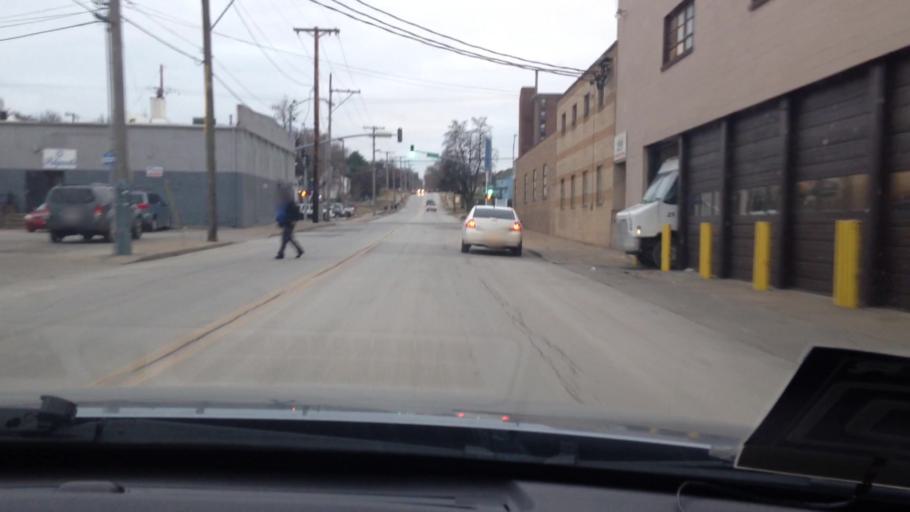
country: US
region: Missouri
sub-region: Clay County
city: North Kansas City
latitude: 39.0948
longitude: -94.5332
